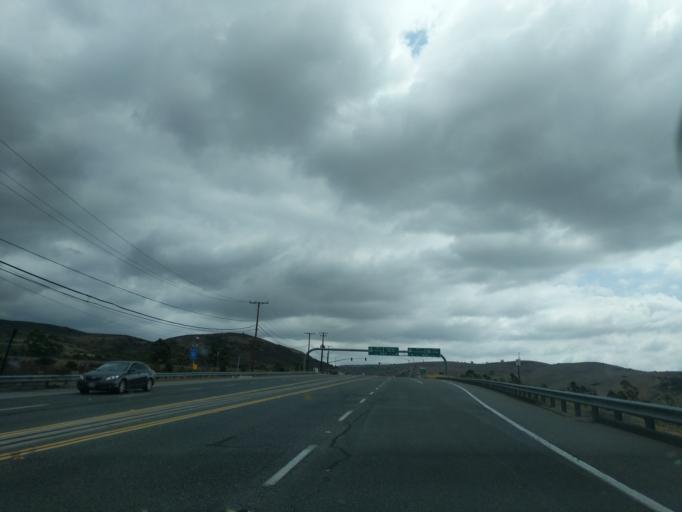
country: US
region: California
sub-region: Orange County
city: North Tustin
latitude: 33.7849
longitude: -117.7510
